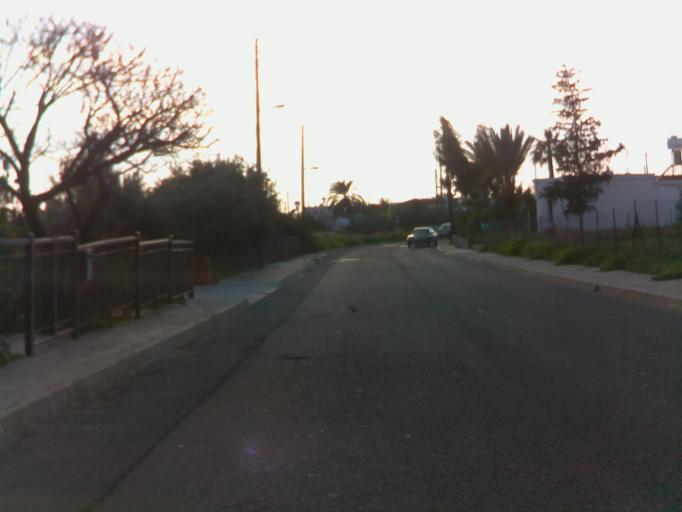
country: CY
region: Pafos
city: Paphos
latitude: 34.7831
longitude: 32.4208
